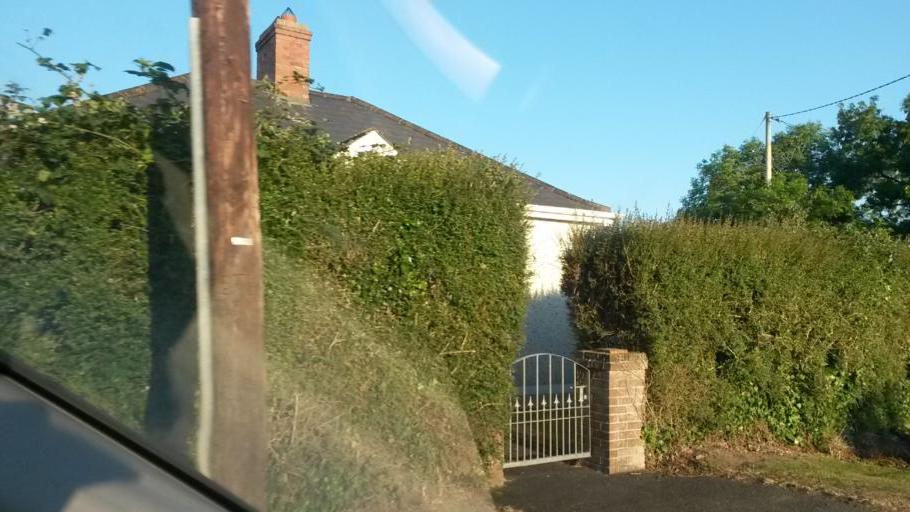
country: IE
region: Leinster
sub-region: An Mhi
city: Ashbourne
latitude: 53.5527
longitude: -6.3592
